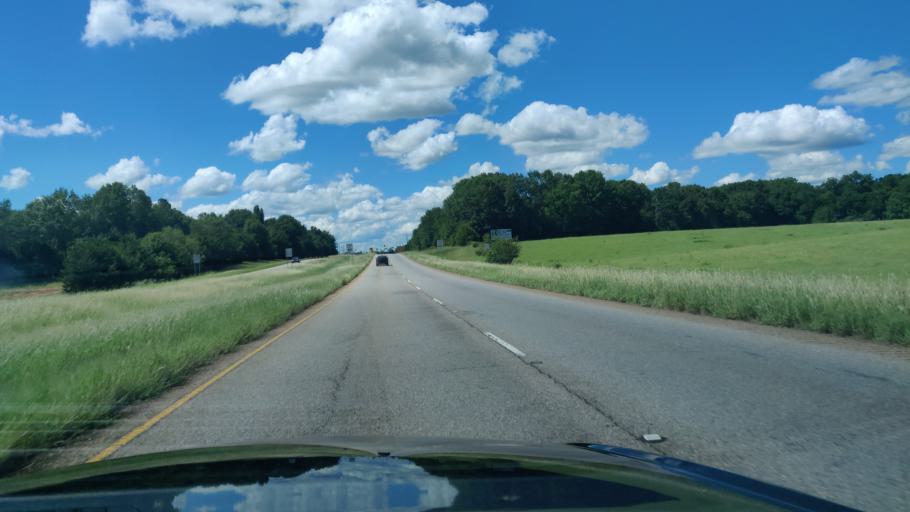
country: US
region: Georgia
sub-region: Stewart County
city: Richland
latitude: 32.0811
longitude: -84.6745
